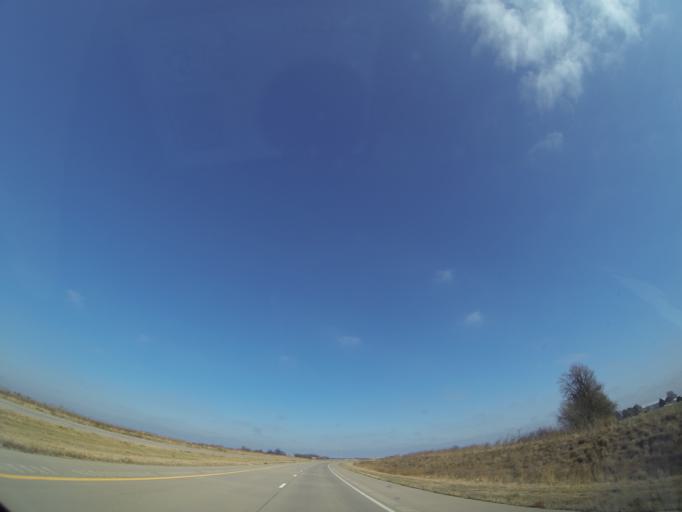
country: US
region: Kansas
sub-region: McPherson County
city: Inman
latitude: 38.2390
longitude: -97.7808
